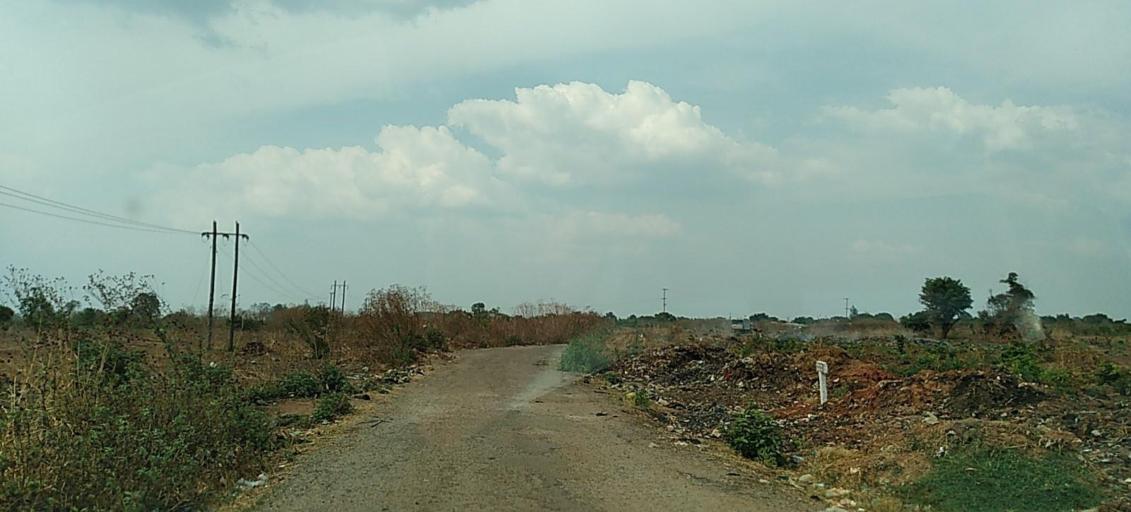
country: ZM
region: Copperbelt
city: Chililabombwe
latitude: -12.3755
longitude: 27.8138
